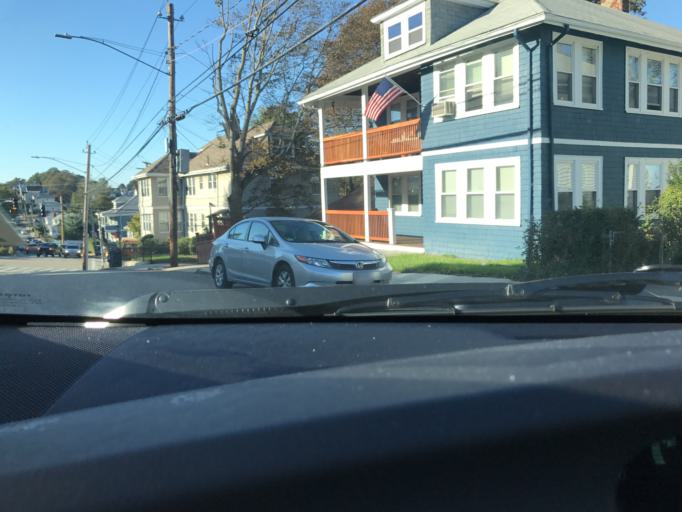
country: US
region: Massachusetts
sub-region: Suffolk County
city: Jamaica Plain
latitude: 42.2730
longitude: -71.1288
